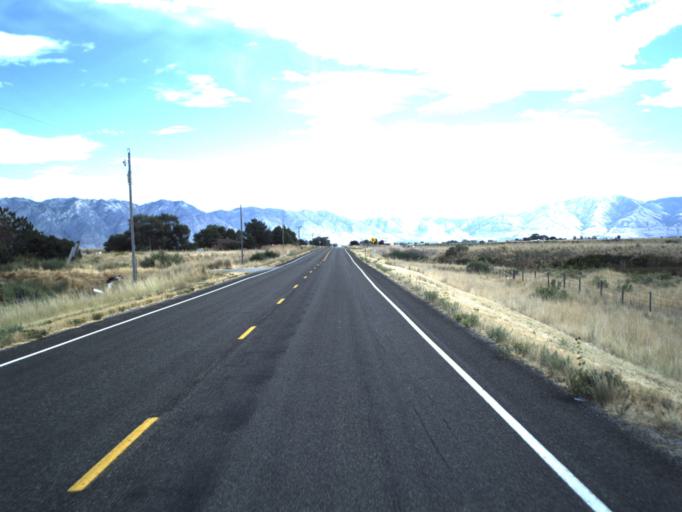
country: US
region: Utah
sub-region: Box Elder County
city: Elwood
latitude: 41.5739
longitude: -112.2205
